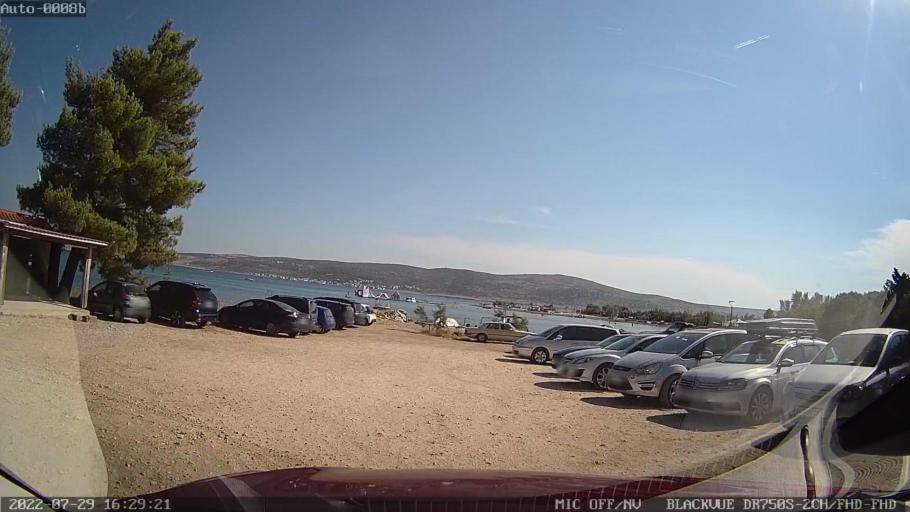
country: HR
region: Zadarska
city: Starigrad
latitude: 44.2833
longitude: 15.4608
